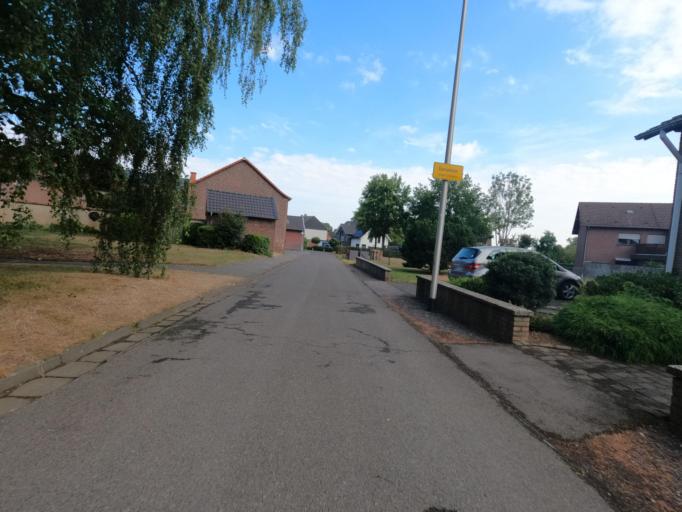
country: DE
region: North Rhine-Westphalia
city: Wegberg
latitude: 51.1091
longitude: 6.2612
